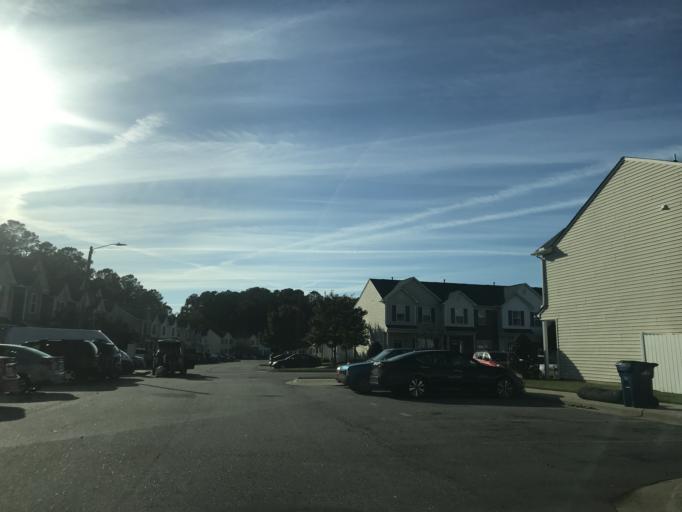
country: US
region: North Carolina
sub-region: Wake County
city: Rolesville
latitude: 35.8935
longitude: -78.5390
